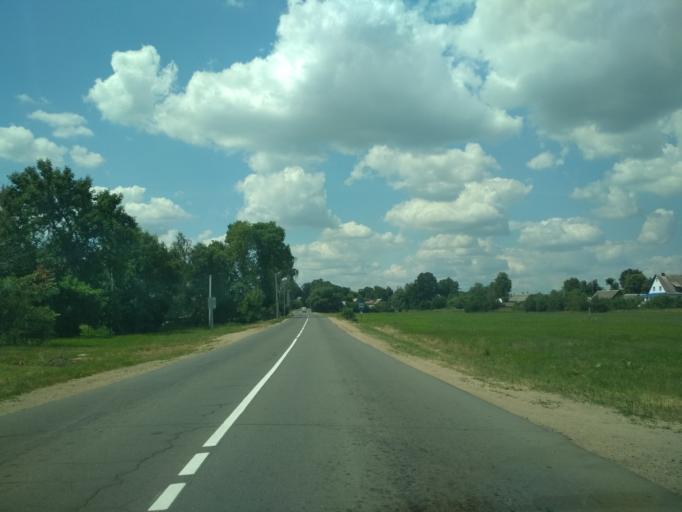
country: BY
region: Minsk
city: Svislach
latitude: 53.5704
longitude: 27.9887
